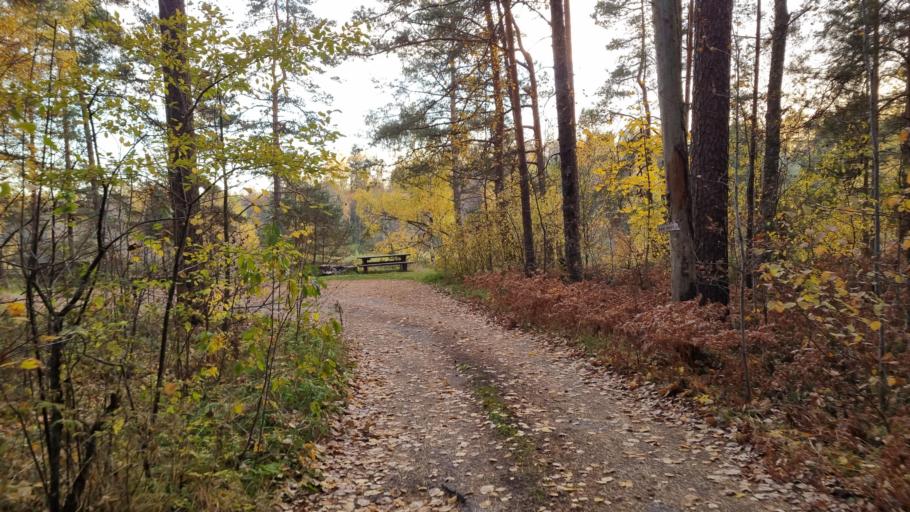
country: LV
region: Strenci
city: Seda
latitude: 57.6278
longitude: 25.7411
